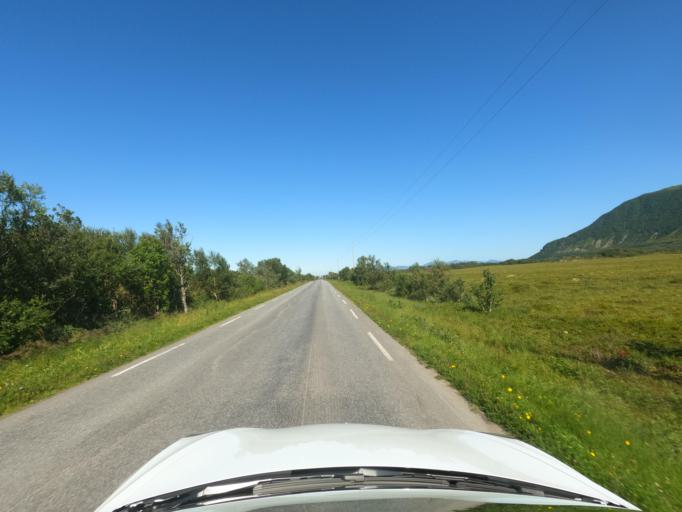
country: NO
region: Nordland
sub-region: Vagan
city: Kabelvag
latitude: 68.3856
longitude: 14.4619
